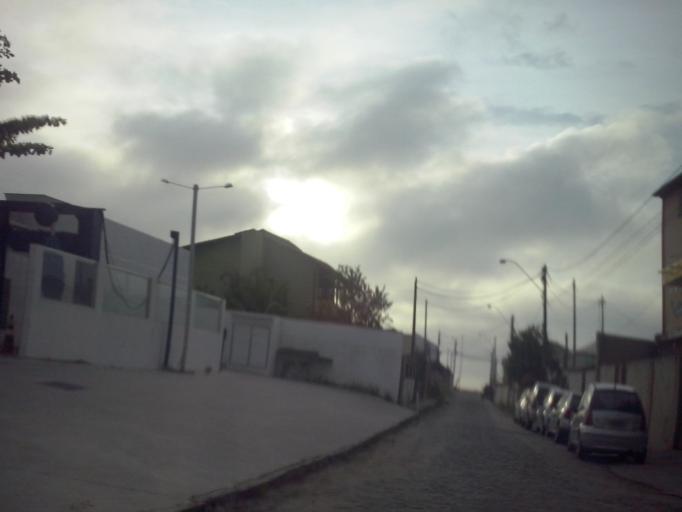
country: BR
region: Rio de Janeiro
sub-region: Rio Das Ostras
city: Rio das Ostras
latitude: -22.5768
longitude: -41.9869
